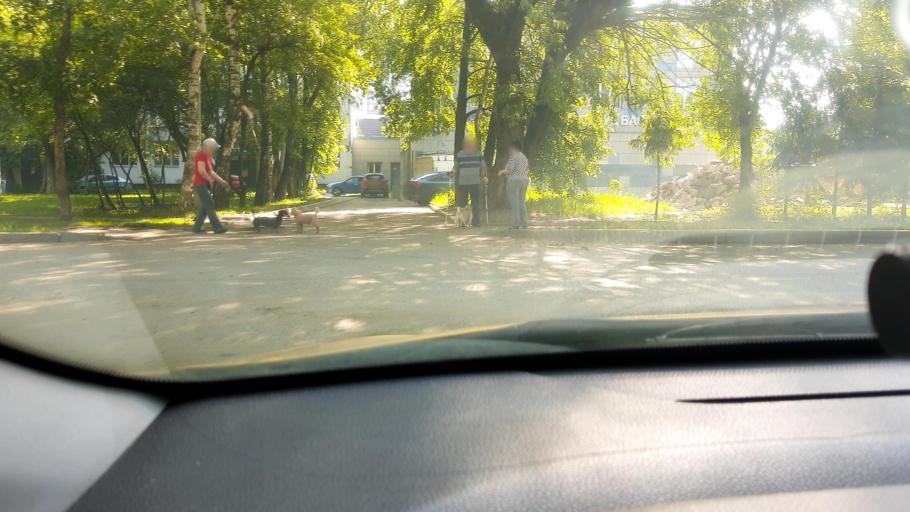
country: RU
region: Moskovskaya
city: Shcherbinka
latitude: 55.5135
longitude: 37.5705
